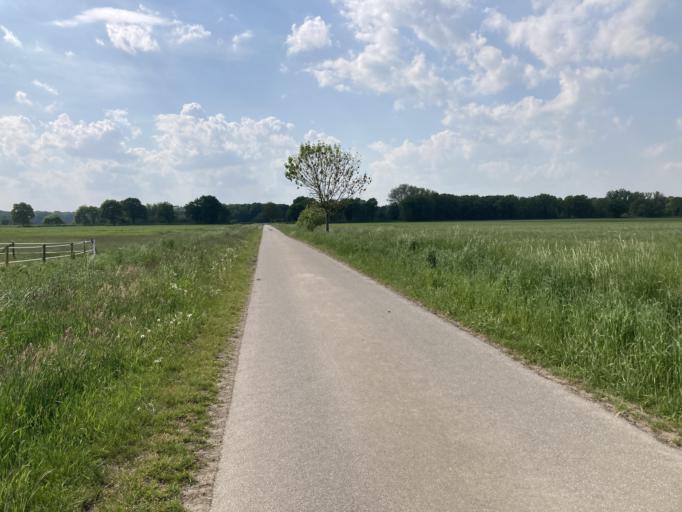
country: DE
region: Lower Saxony
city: Brietlingen
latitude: 53.3556
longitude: 10.4494
